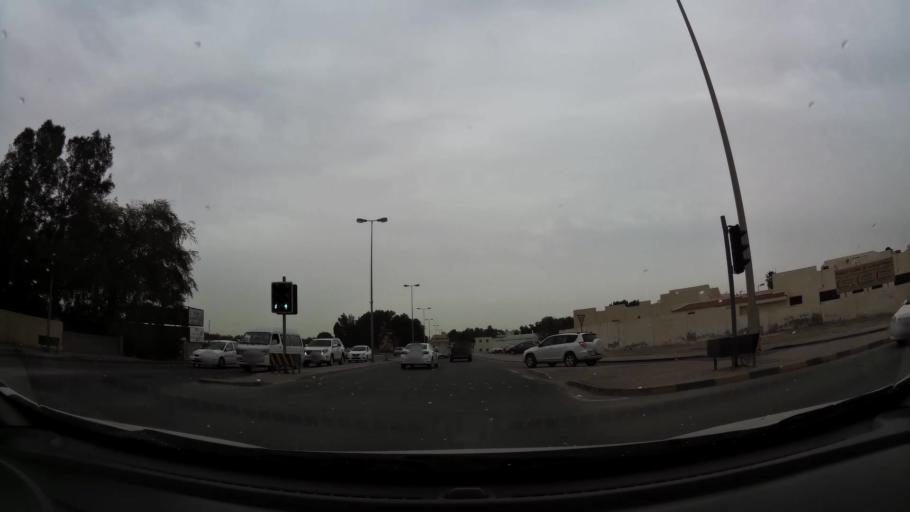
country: BH
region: Manama
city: Jidd Hafs
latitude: 26.2093
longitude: 50.5339
